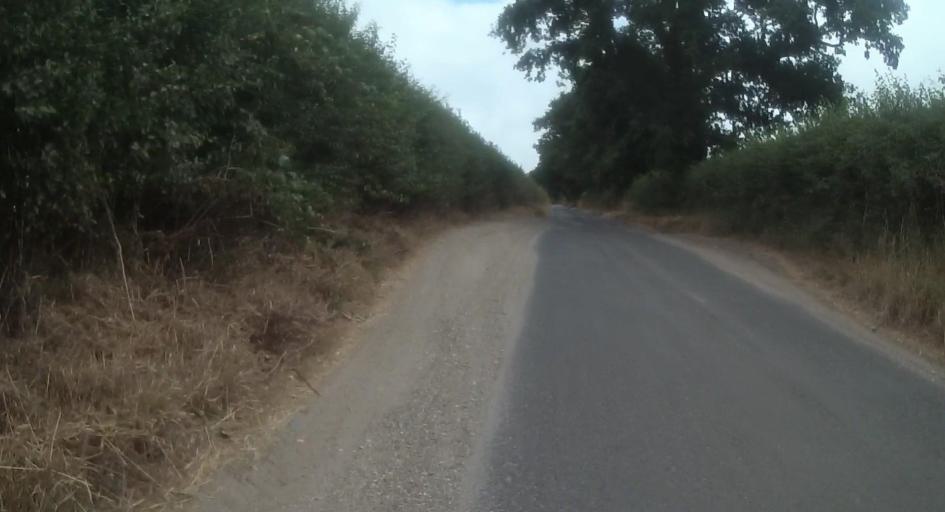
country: GB
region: England
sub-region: Dorset
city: Bovington Camp
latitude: 50.7068
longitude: -2.2877
